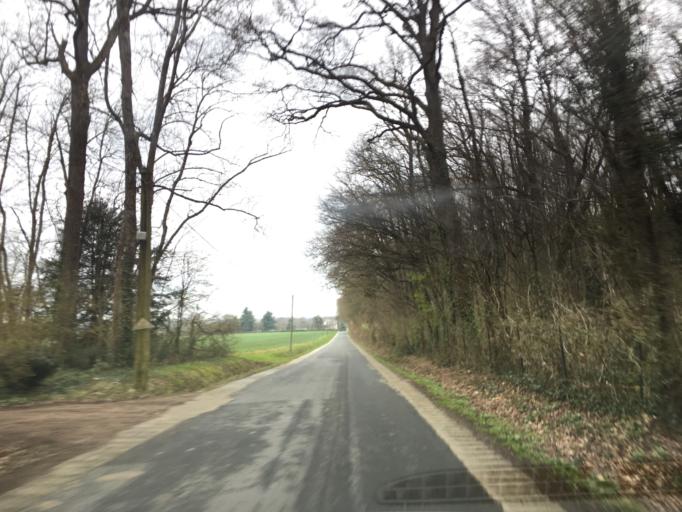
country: FR
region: Centre
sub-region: Departement d'Indre-et-Loire
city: Chanceaux-sur-Choisille
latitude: 47.4716
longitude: 0.7307
